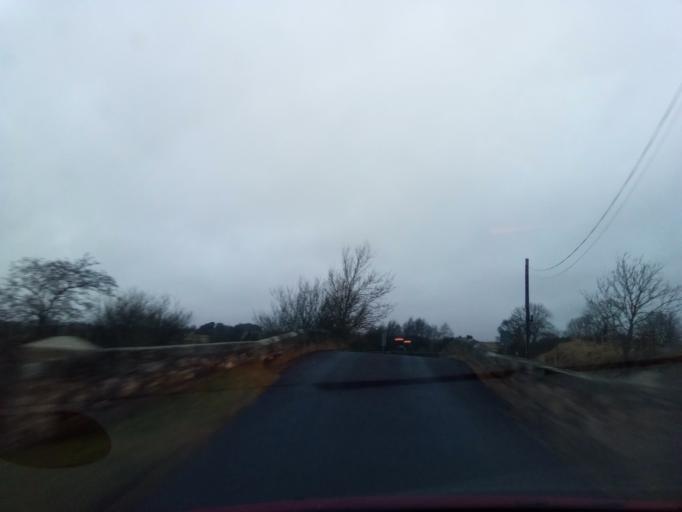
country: GB
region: England
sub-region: Northumberland
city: Otterburn
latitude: 55.2298
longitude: -2.1030
